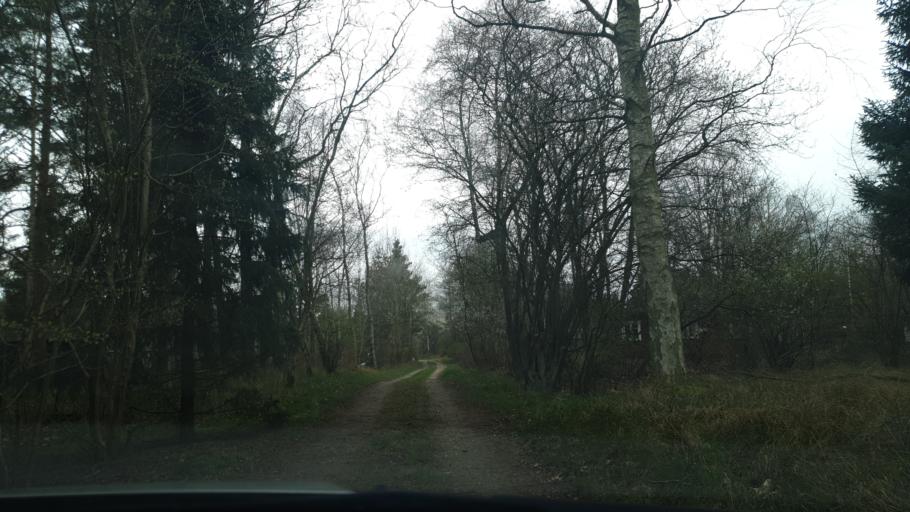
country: DK
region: Zealand
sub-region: Odsherred Kommune
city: Asnaes
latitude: 55.8343
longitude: 11.4180
